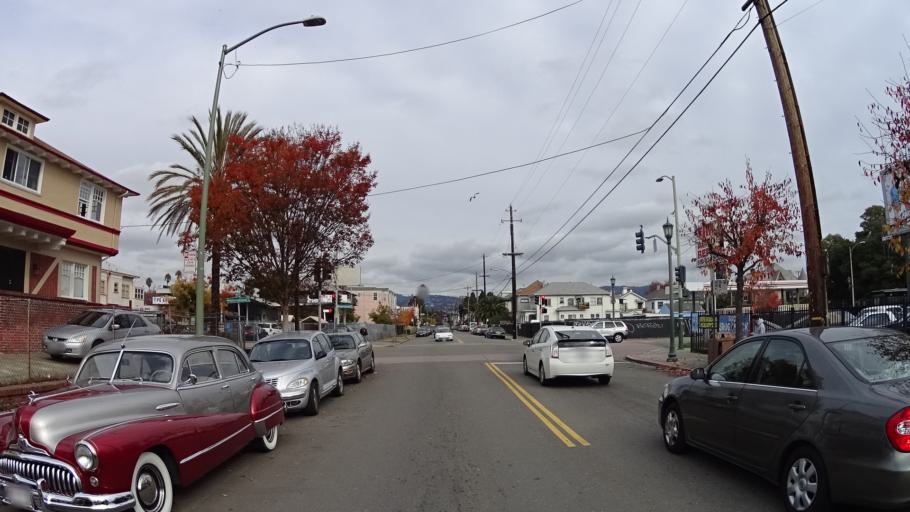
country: US
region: California
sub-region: Alameda County
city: Oakland
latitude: 37.7955
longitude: -122.2542
